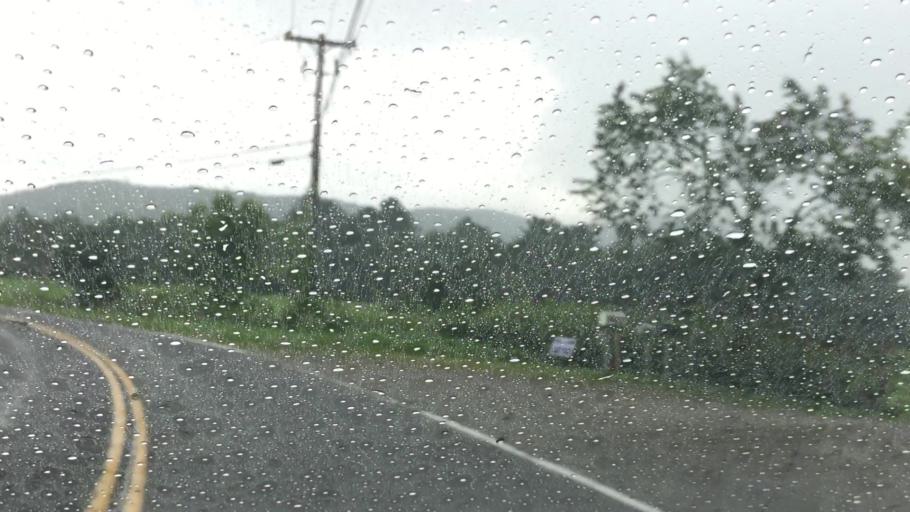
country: US
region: Massachusetts
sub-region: Berkshire County
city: Housatonic
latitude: 42.2935
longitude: -73.4028
